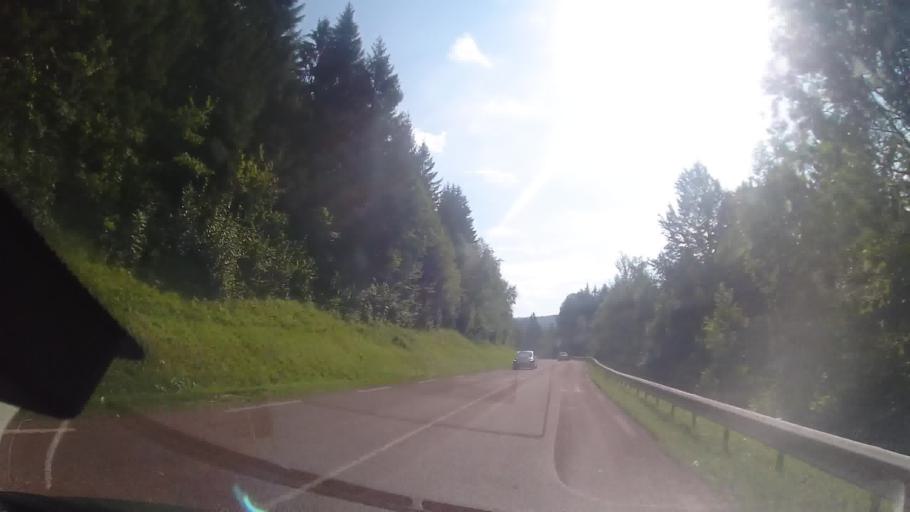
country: FR
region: Franche-Comte
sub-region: Departement du Jura
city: Morbier
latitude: 46.5989
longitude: 5.9117
